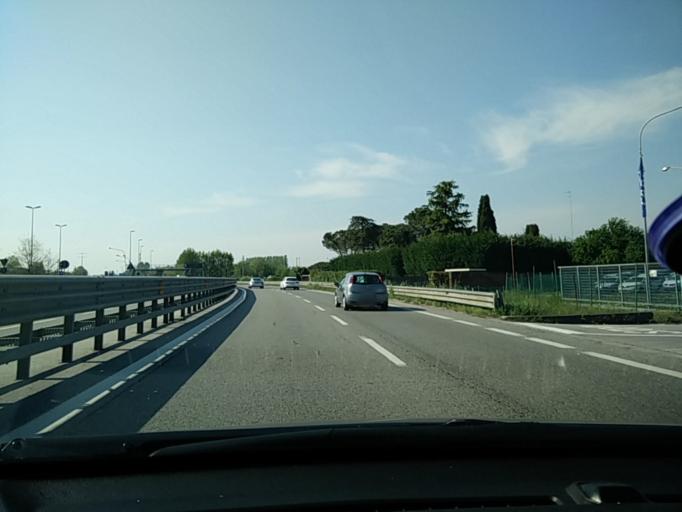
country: IT
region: Veneto
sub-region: Provincia di Venezia
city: Campalto
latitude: 45.5062
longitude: 12.2708
